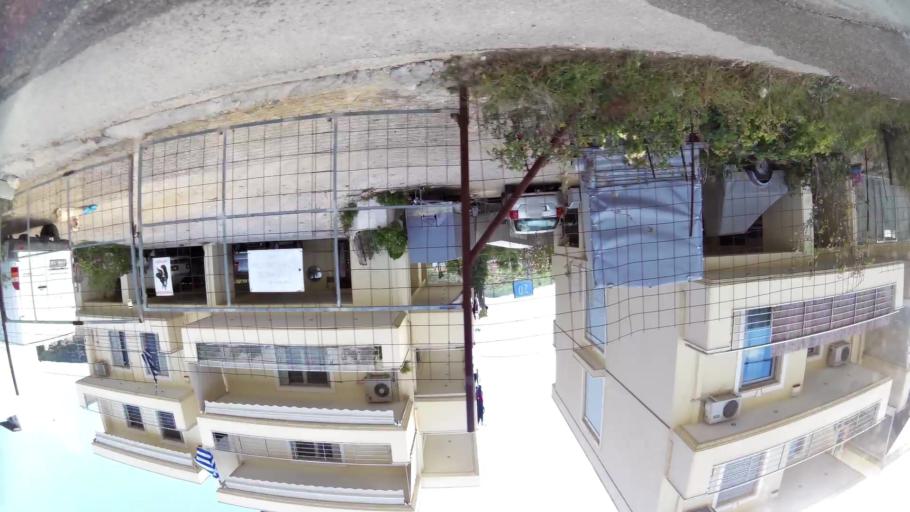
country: GR
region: Attica
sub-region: Nomarchia Anatolikis Attikis
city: Thrakomakedones
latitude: 38.1152
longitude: 23.7304
